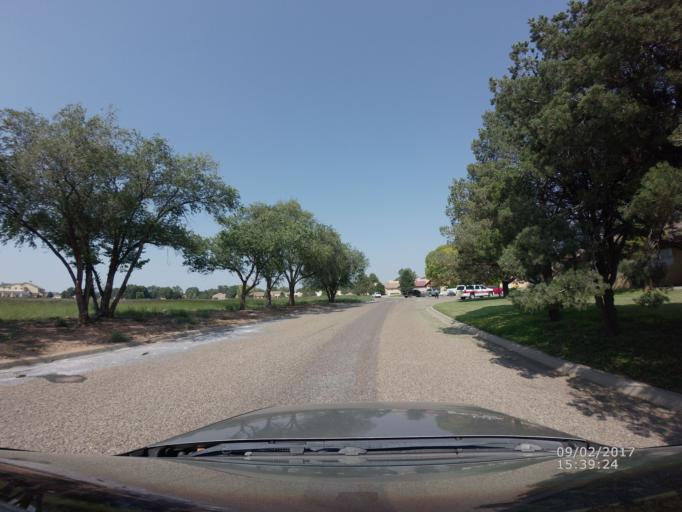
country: US
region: New Mexico
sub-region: Curry County
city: Clovis
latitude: 34.4407
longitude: -103.1950
